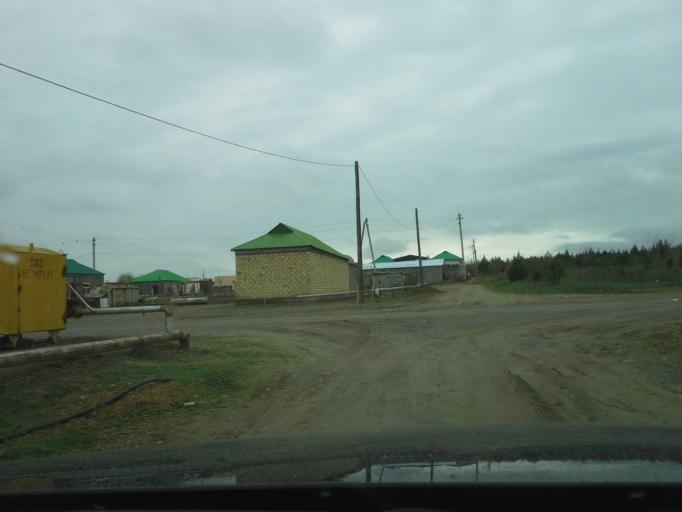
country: TM
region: Ahal
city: Abadan
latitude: 37.9594
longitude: 58.2289
